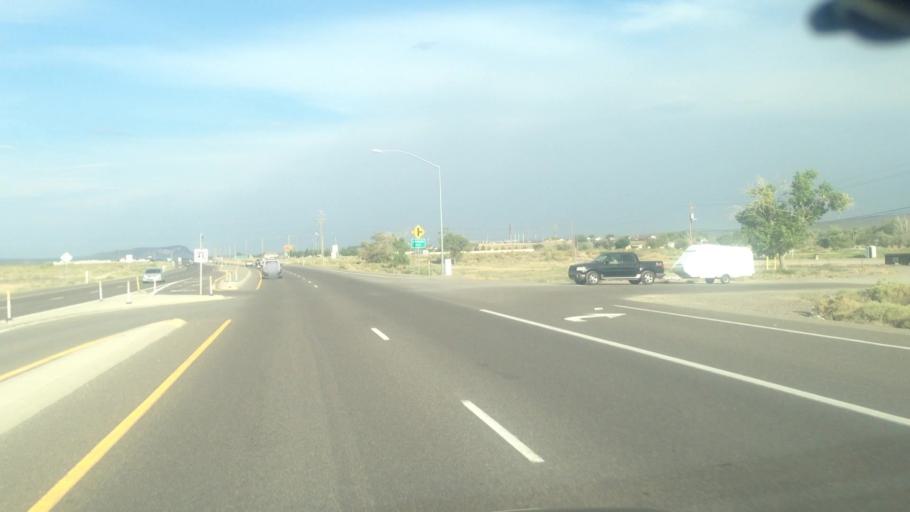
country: US
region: Nevada
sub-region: Lyon County
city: Fernley
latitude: 39.6015
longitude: -119.2203
